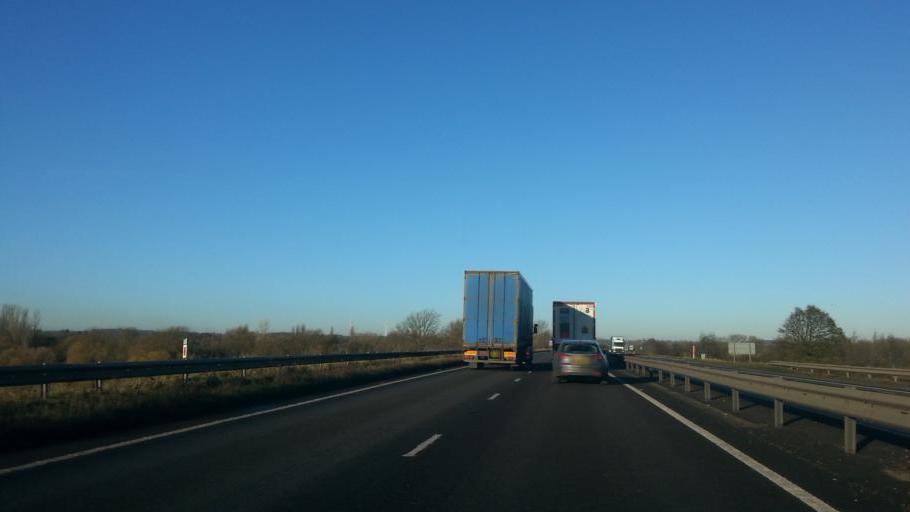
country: GB
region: England
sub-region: Nottinghamshire
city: Newark on Trent
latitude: 53.1036
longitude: -0.8029
